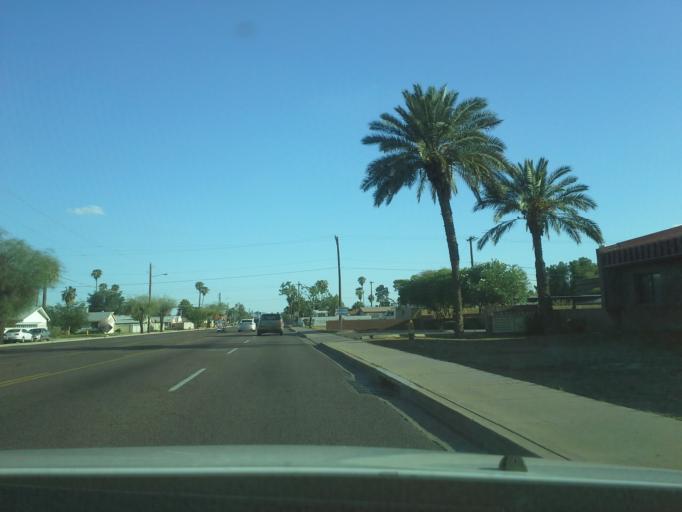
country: US
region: Arizona
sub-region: Maricopa County
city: Glendale
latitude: 33.5637
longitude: -112.1343
